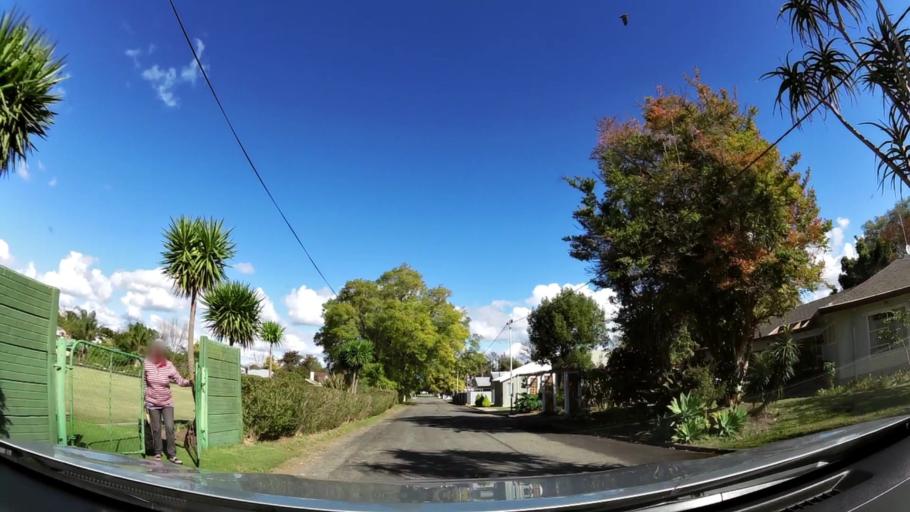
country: ZA
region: Western Cape
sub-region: Overberg District Municipality
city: Swellendam
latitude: -34.0214
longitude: 20.4477
